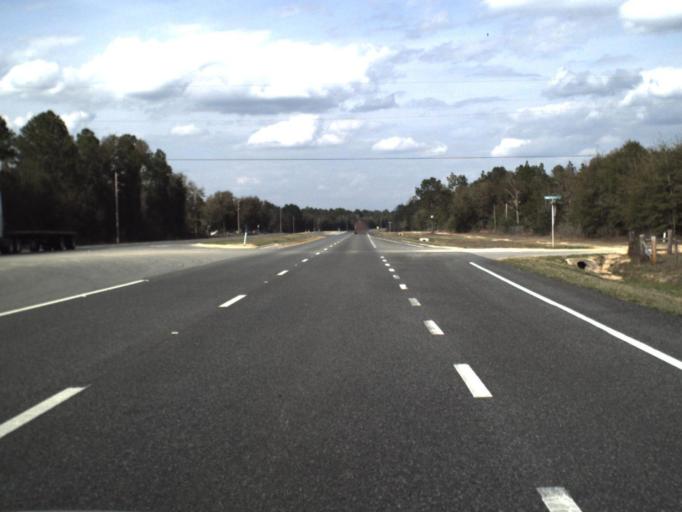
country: US
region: Florida
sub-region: Bay County
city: Youngstown
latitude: 30.5157
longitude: -85.4096
